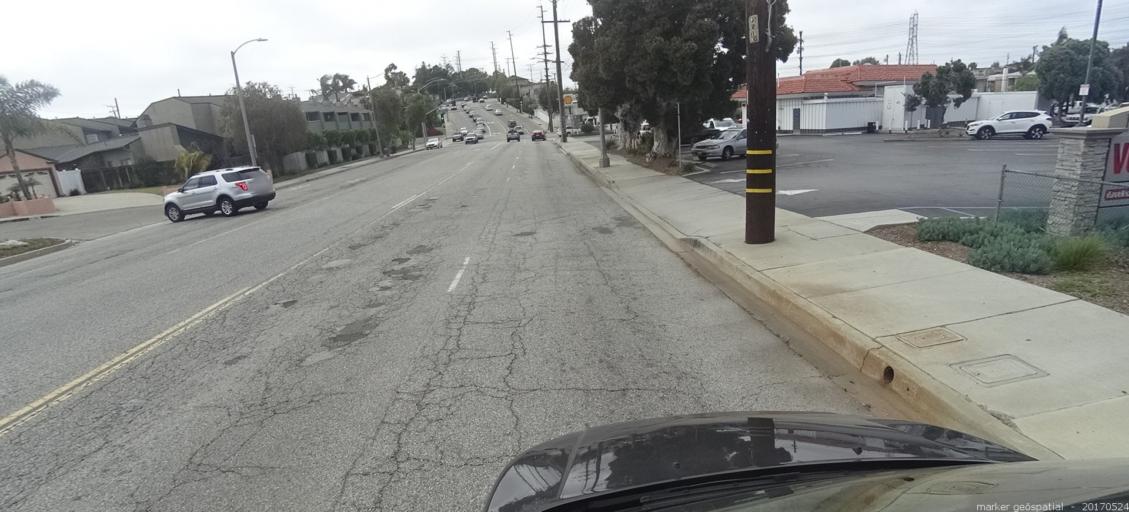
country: US
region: California
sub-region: Los Angeles County
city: Redondo Beach
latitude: 33.8536
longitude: -118.3811
